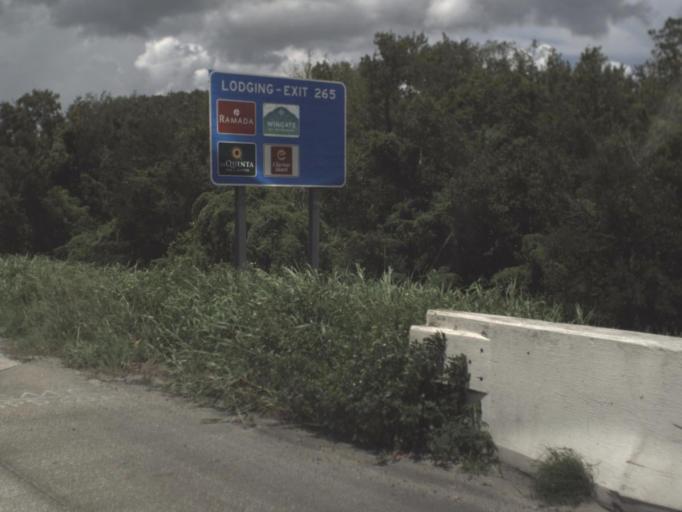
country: US
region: Florida
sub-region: Hillsborough County
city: Temple Terrace
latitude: 28.0304
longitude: -82.3429
